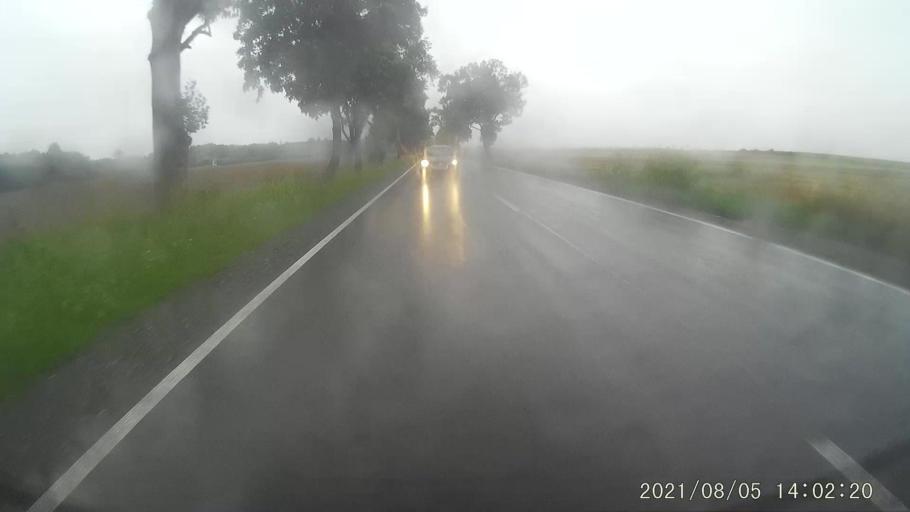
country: PL
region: Opole Voivodeship
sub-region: Powiat krapkowicki
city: Strzeleczki
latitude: 50.4548
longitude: 17.8767
